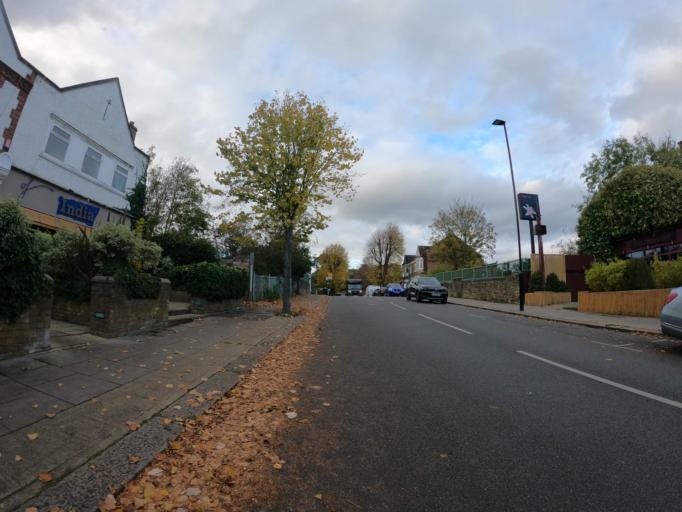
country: GB
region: England
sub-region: Greater London
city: Isleworth
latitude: 51.4829
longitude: -0.3479
